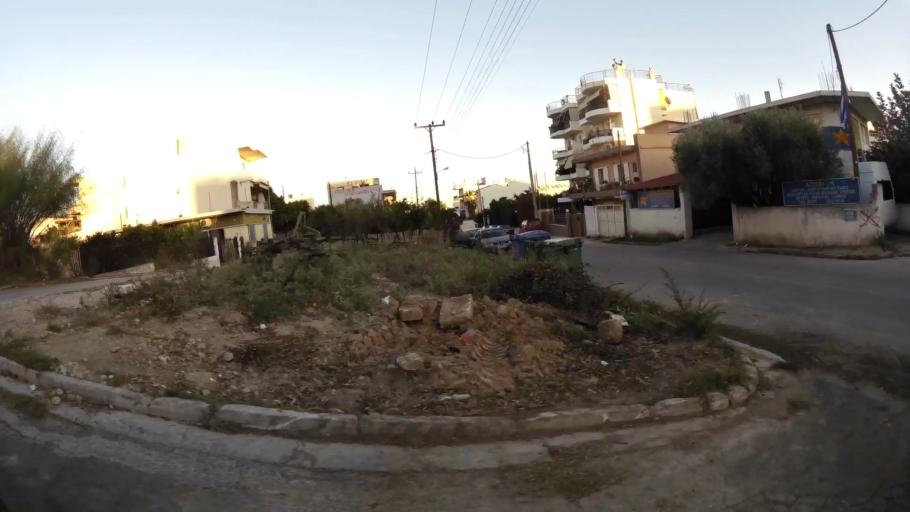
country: GR
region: Attica
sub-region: Nomarchia Anatolikis Attikis
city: Spata
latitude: 37.9660
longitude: 23.9185
